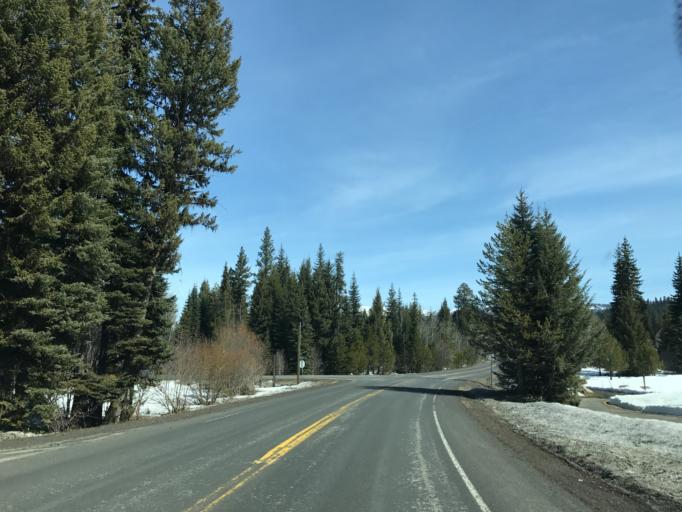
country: US
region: Idaho
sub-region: Valley County
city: McCall
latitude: 44.9108
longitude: -116.0812
